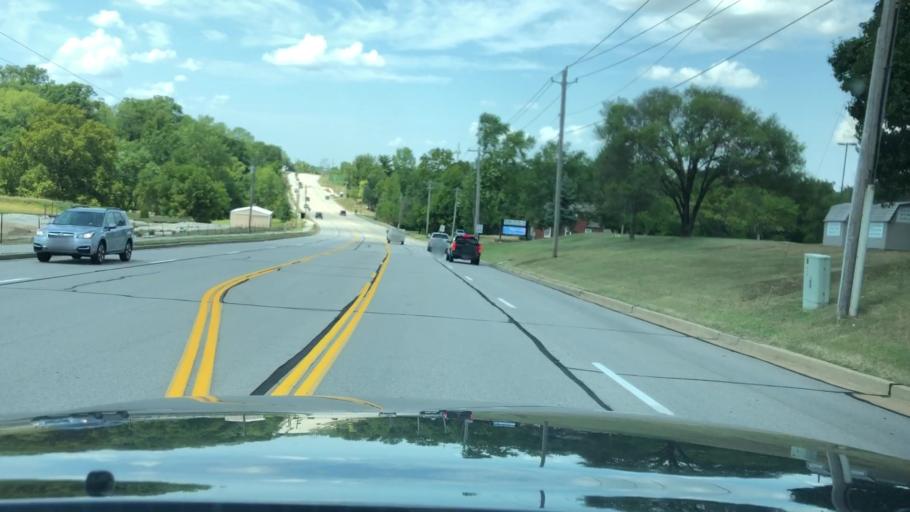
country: US
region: Missouri
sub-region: Saint Charles County
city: O'Fallon
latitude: 38.7911
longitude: -90.6837
